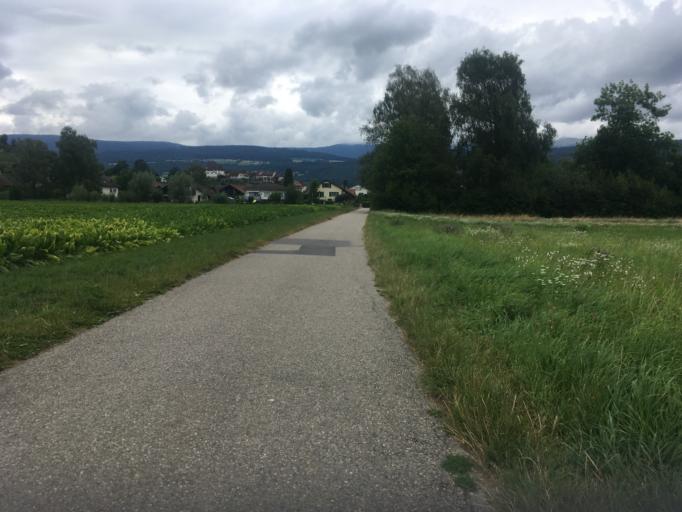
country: CH
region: Bern
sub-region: Seeland District
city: Erlach
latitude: 47.0394
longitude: 7.1031
